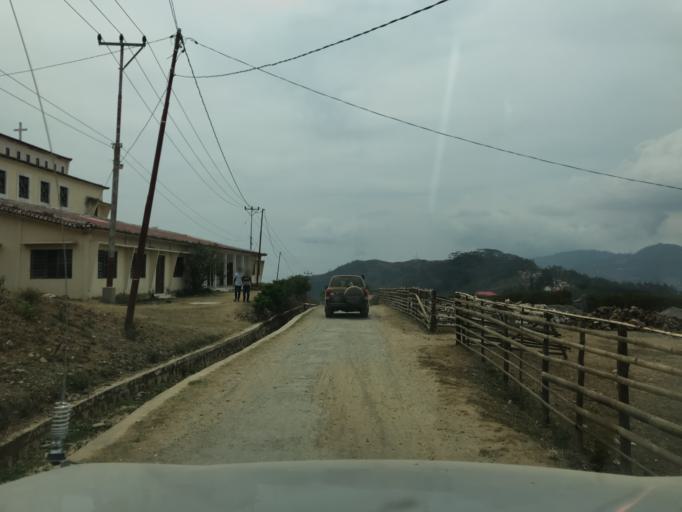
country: TL
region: Ermera
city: Gleno
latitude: -8.8373
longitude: 125.4319
